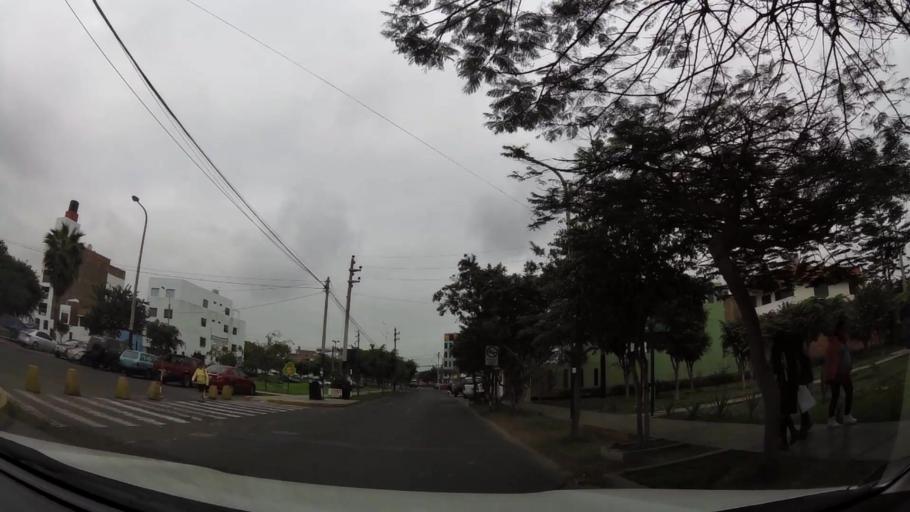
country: PE
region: Lima
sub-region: Lima
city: Surco
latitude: -12.1635
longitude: -76.9964
